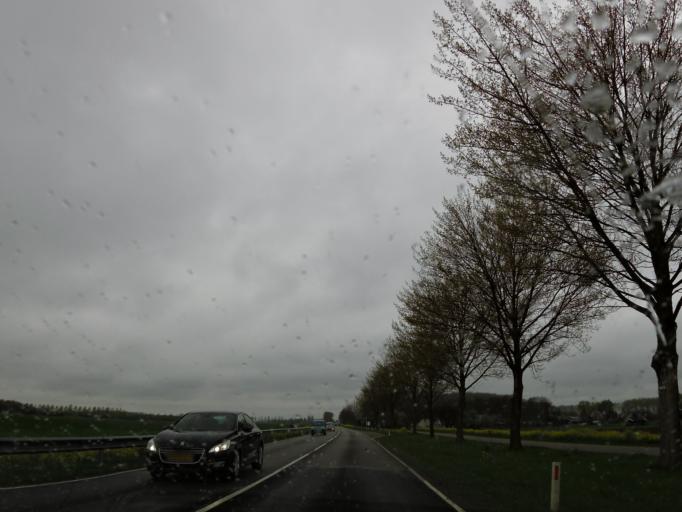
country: NL
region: Gelderland
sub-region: Gemeente Culemborg
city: Culemborg
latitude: 51.9351
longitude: 5.1816
